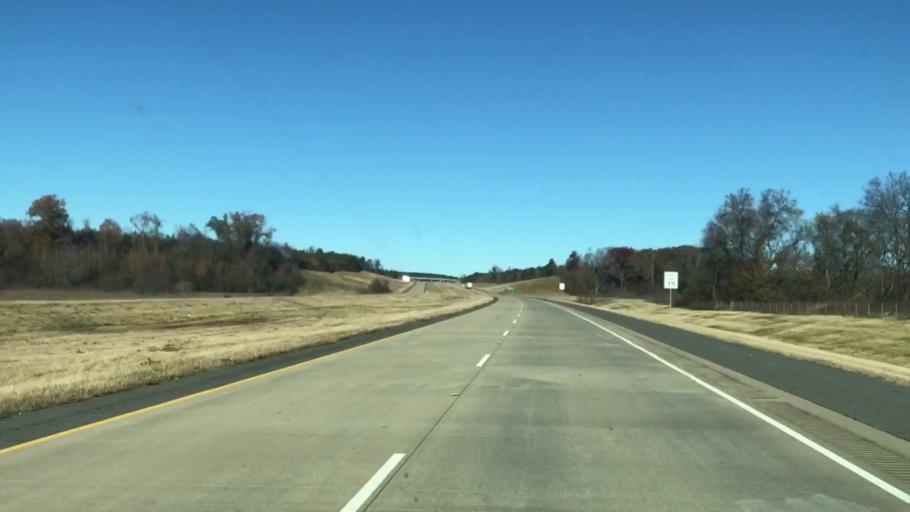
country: US
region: Louisiana
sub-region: Caddo Parish
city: Vivian
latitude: 32.9089
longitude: -93.8688
